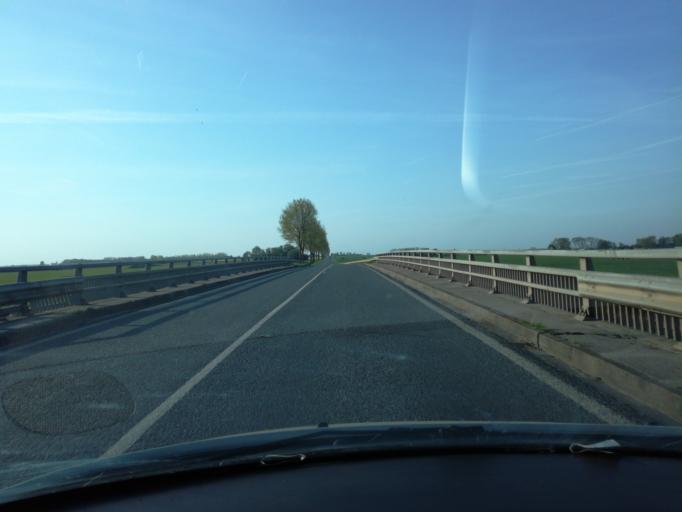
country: FR
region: Picardie
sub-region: Departement de la Somme
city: Poix-de-Picardie
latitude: 49.8104
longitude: 1.9647
